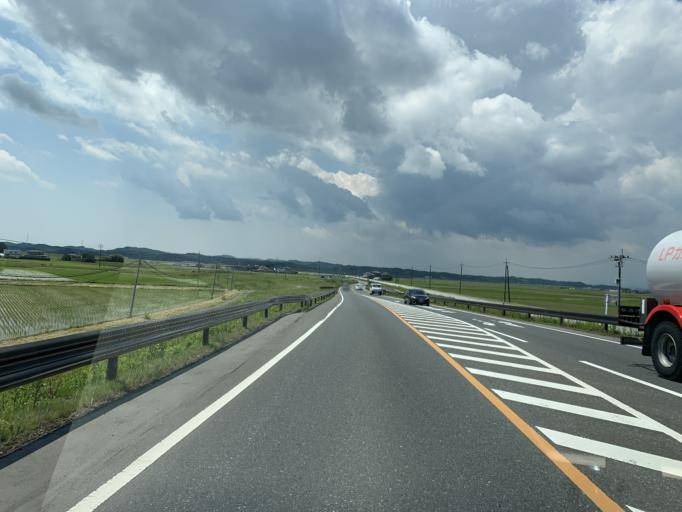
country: JP
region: Miyagi
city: Matsushima
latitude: 38.4543
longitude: 141.0860
